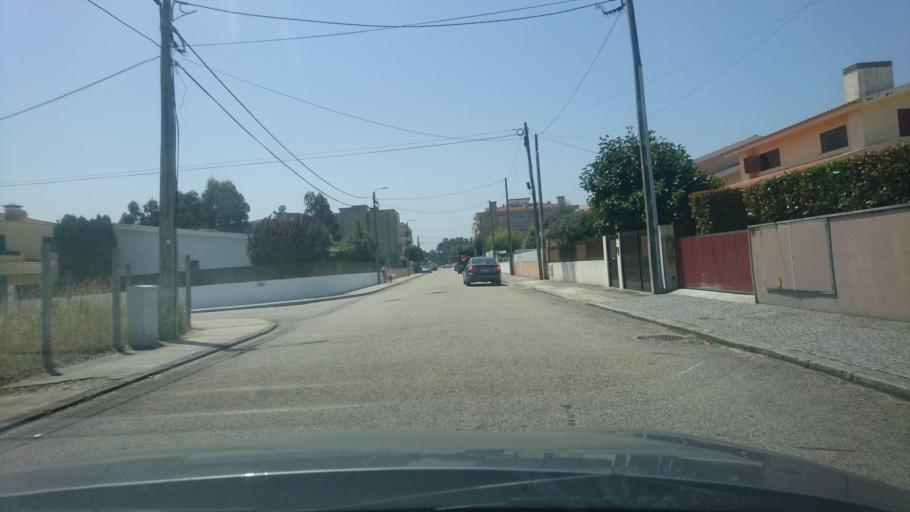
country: PT
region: Aveiro
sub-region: Ovar
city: Esmoriz
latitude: 40.9561
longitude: -8.6426
